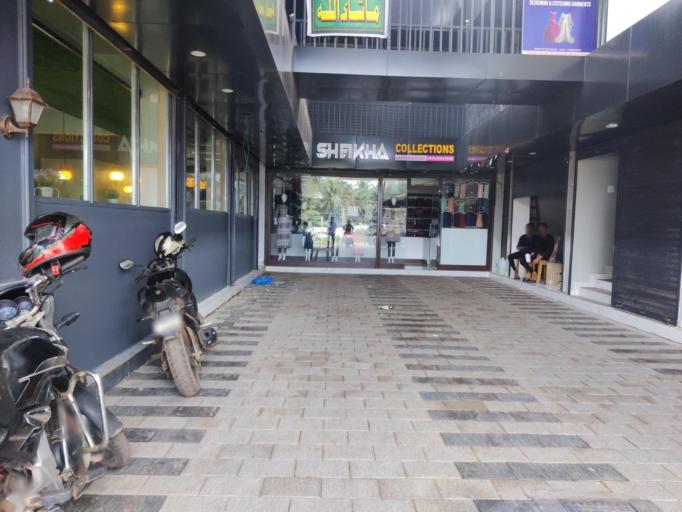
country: IN
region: Kerala
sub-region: Kasaragod District
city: Kasaragod
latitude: 12.4292
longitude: 75.0733
